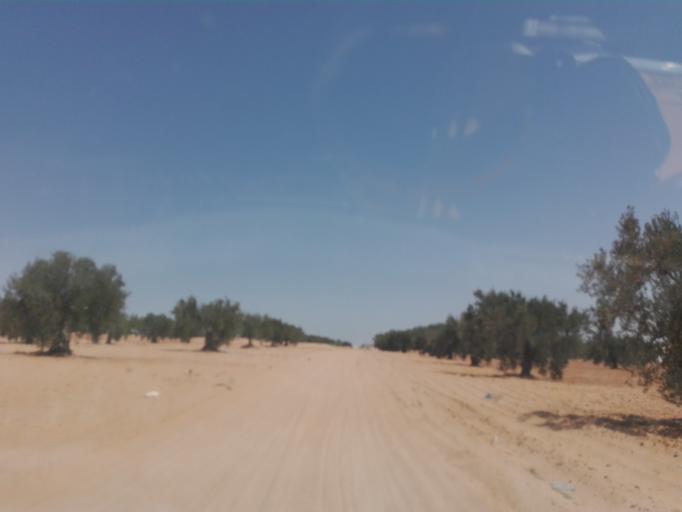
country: TN
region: Safaqis
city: Bi'r `Ali Bin Khalifah
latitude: 34.6520
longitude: 10.2481
